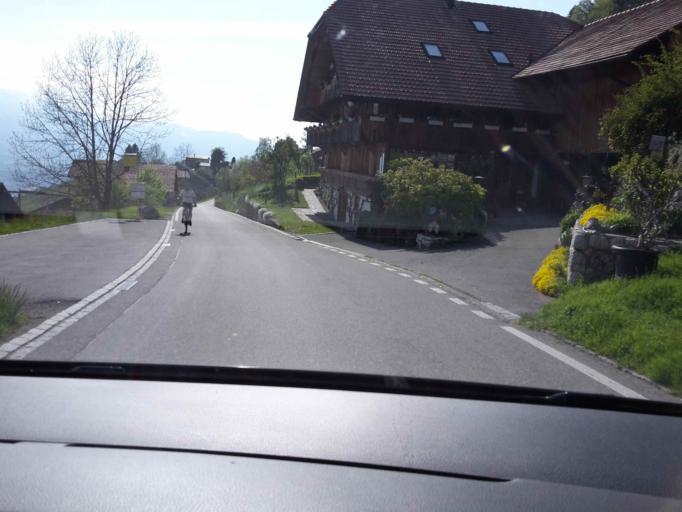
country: CH
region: Bern
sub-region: Thun District
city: Hilterfingen
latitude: 46.7633
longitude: 7.6798
